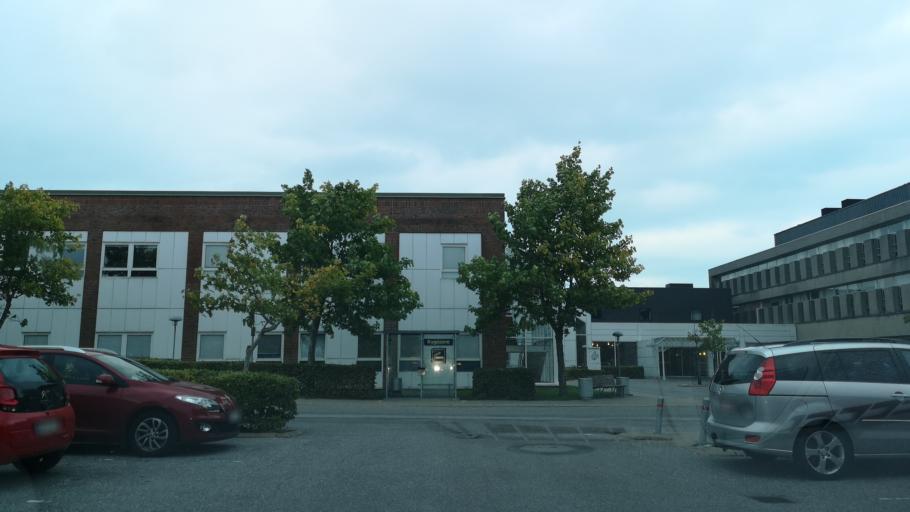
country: DK
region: Central Jutland
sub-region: Herning Kommune
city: Herning
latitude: 56.1392
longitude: 8.9690
